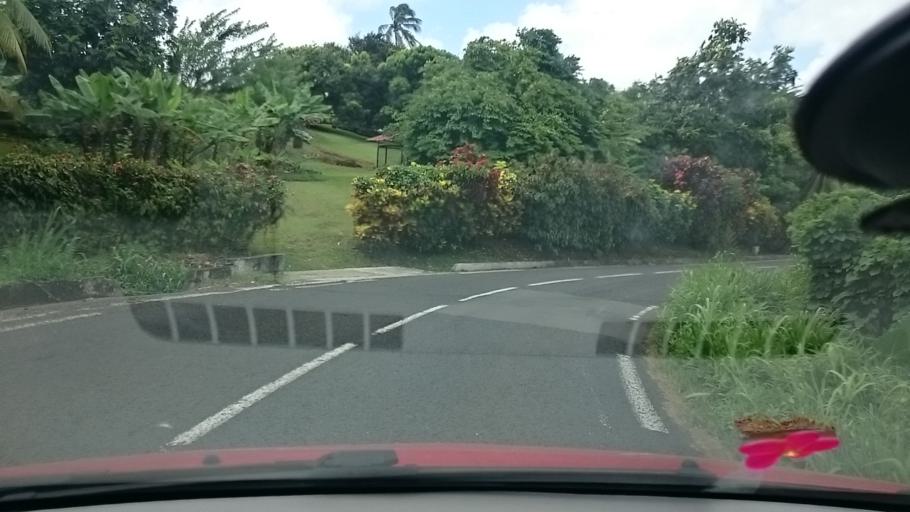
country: MQ
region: Martinique
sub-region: Martinique
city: Le Francois
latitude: 14.5896
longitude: -60.9212
